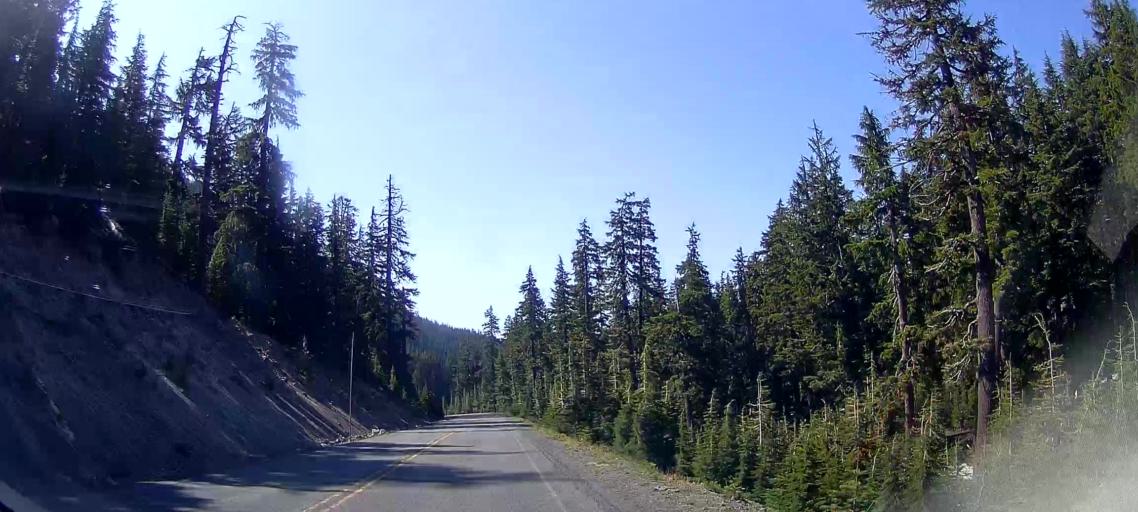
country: US
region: Oregon
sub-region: Jackson County
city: Shady Cove
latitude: 42.9042
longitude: -122.1353
